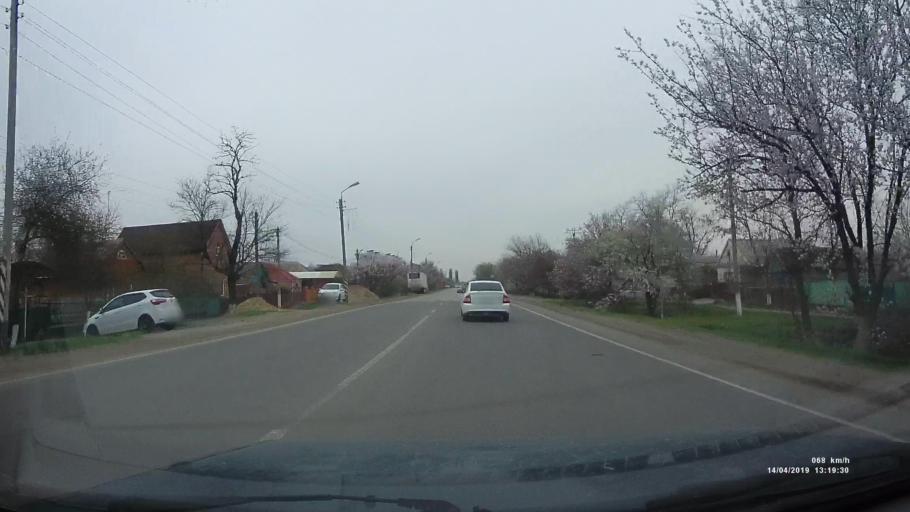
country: RU
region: Rostov
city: Kuleshovka
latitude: 47.0809
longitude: 39.5442
